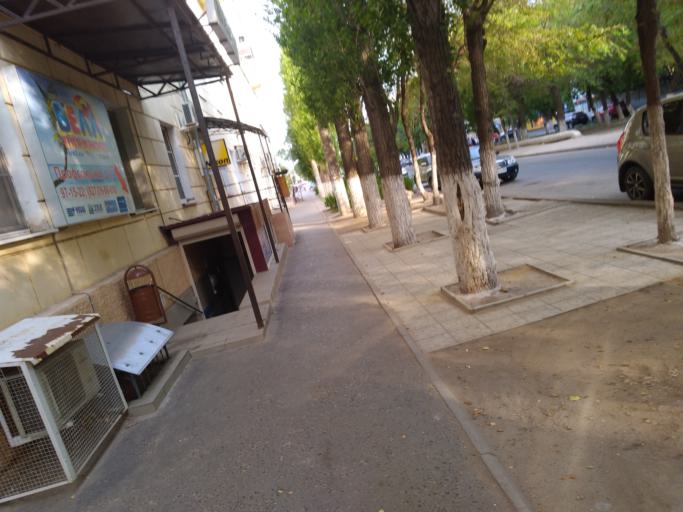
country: RU
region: Volgograd
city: Volgograd
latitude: 48.6982
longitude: 44.4979
